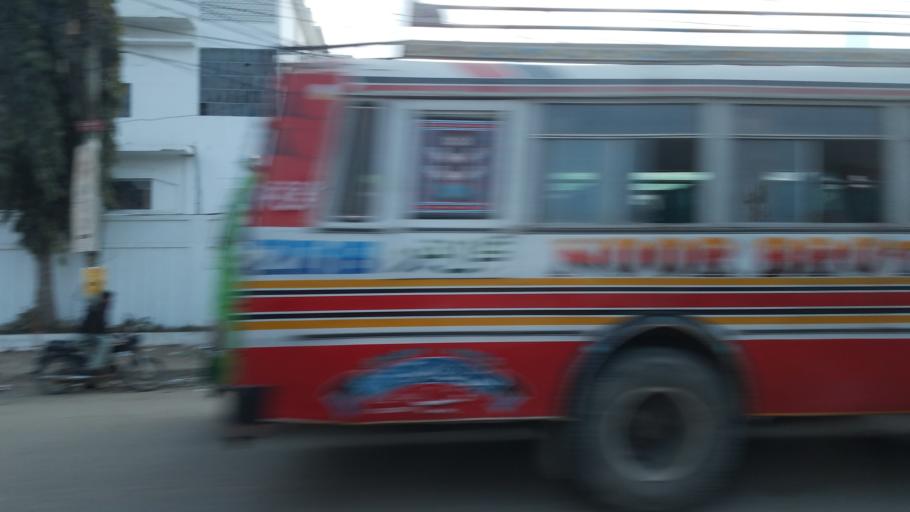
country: PK
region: Sindh
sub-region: Karachi District
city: Karachi
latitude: 24.9355
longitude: 67.0856
